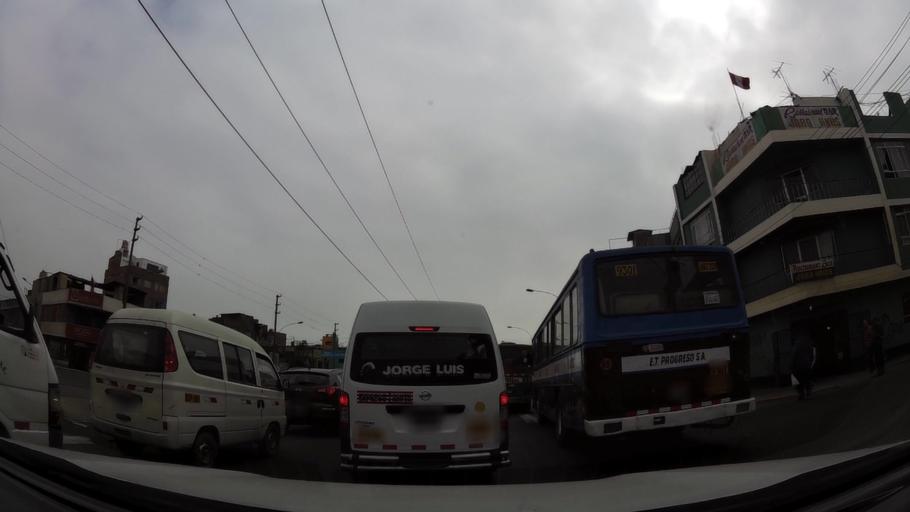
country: PE
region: Callao
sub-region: Callao
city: Callao
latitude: -12.0300
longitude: -77.0932
